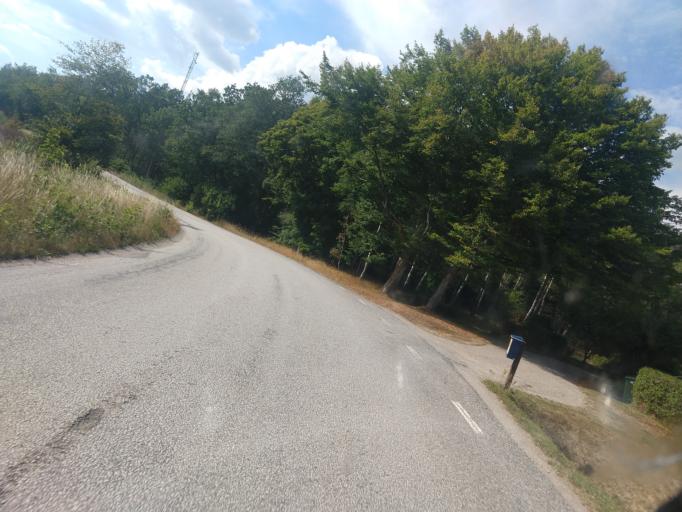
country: SE
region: Blekinge
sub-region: Karlskrona Kommun
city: Rodeby
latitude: 56.2382
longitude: 15.5729
